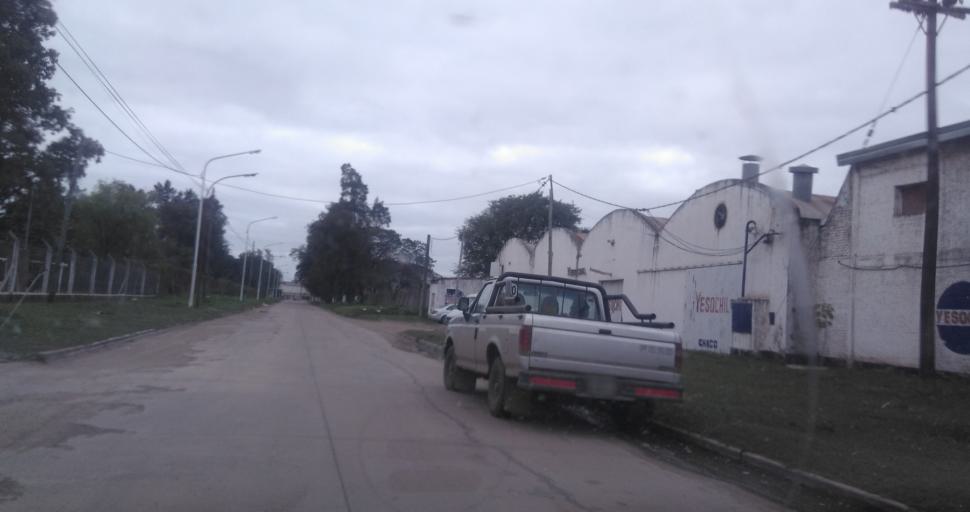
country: AR
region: Chaco
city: Fontana
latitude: -27.4316
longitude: -59.0277
